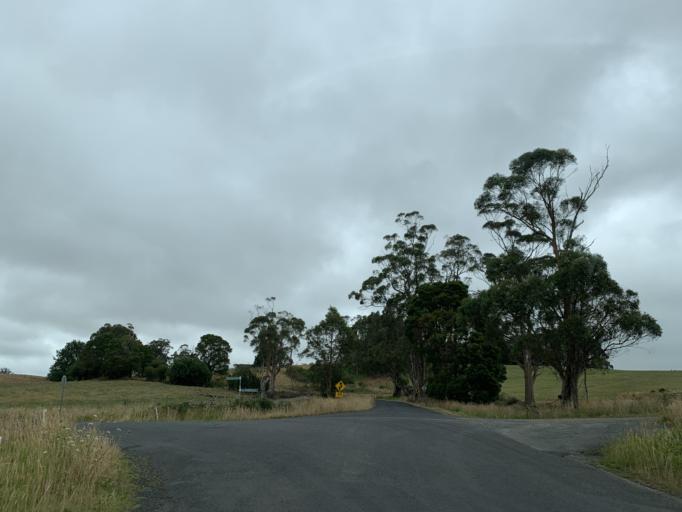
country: AU
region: Victoria
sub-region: Baw Baw
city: Warragul
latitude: -38.2928
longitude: 145.8320
